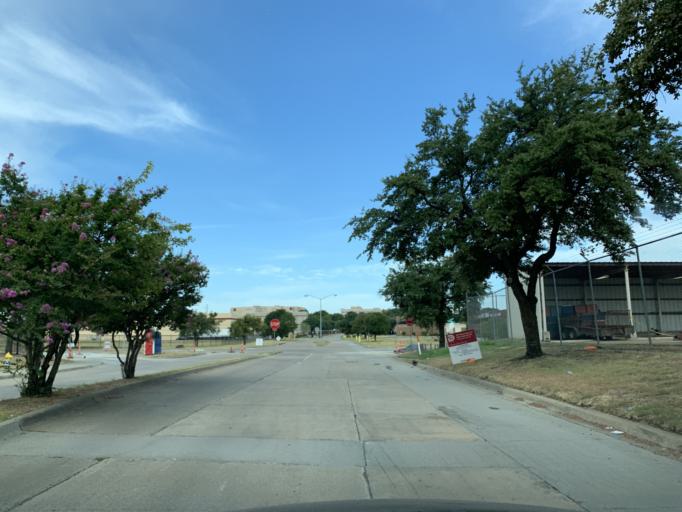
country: US
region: Texas
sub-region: Dallas County
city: Cockrell Hill
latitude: 32.7688
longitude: -96.8617
